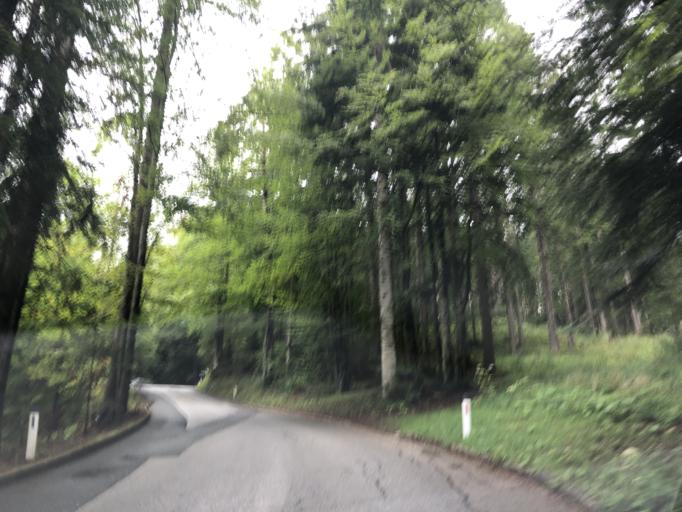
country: AT
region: Tyrol
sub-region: Politischer Bezirk Kufstein
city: Scheffau am Wilden Kaiser
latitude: 47.5353
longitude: 12.2446
